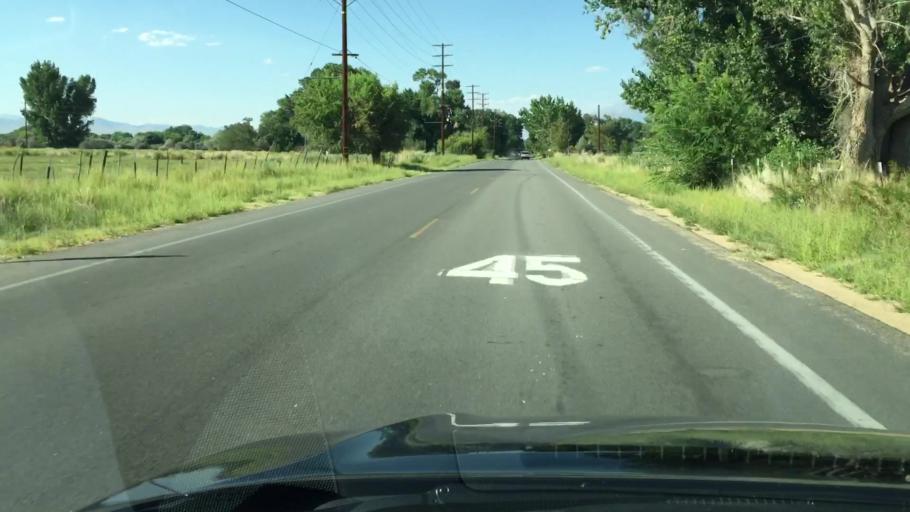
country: US
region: California
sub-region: Inyo County
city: Bishop
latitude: 37.3521
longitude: -118.4046
